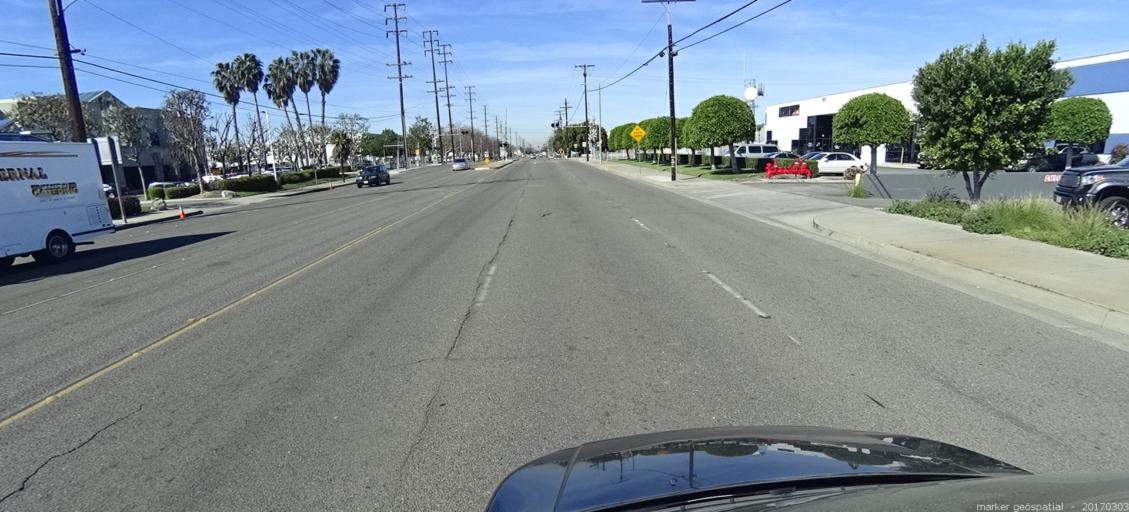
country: US
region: California
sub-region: Orange County
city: Fullerton
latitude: 33.8596
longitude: -117.9101
